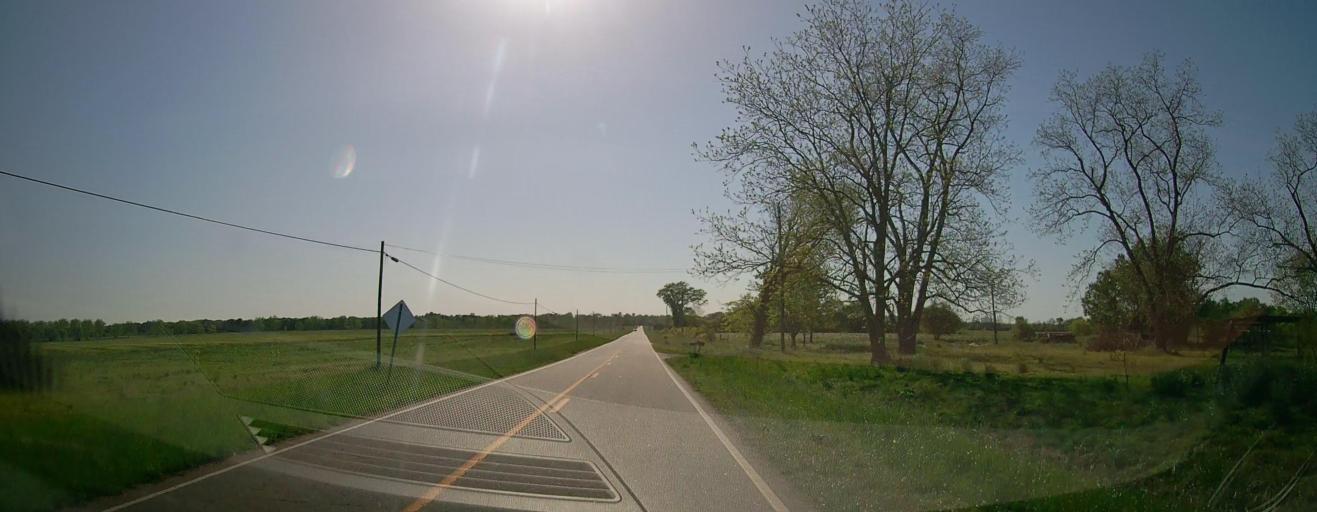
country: US
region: Georgia
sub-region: Houston County
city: Perry
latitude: 32.4515
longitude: -83.6548
